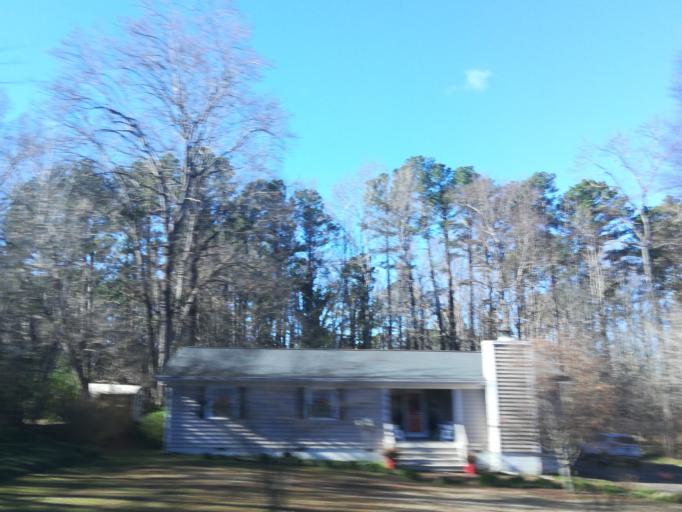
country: US
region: North Carolina
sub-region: Durham County
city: Durham
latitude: 36.0420
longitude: -78.9815
